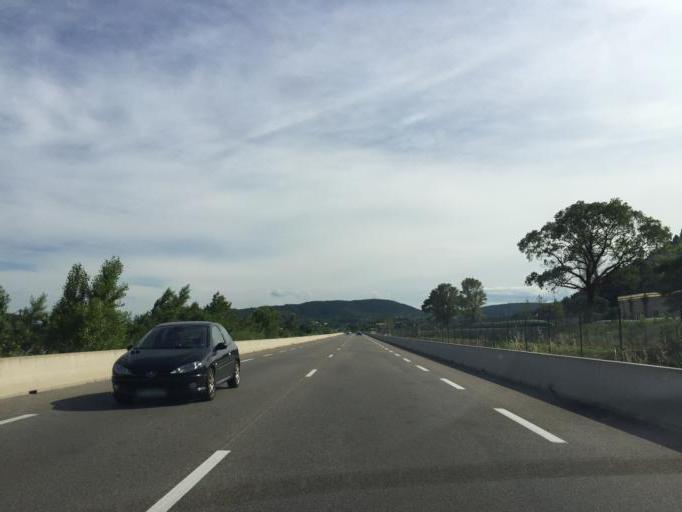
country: FR
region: Rhone-Alpes
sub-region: Departement de l'Ardeche
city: Le Teil
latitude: 44.5607
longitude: 4.6921
